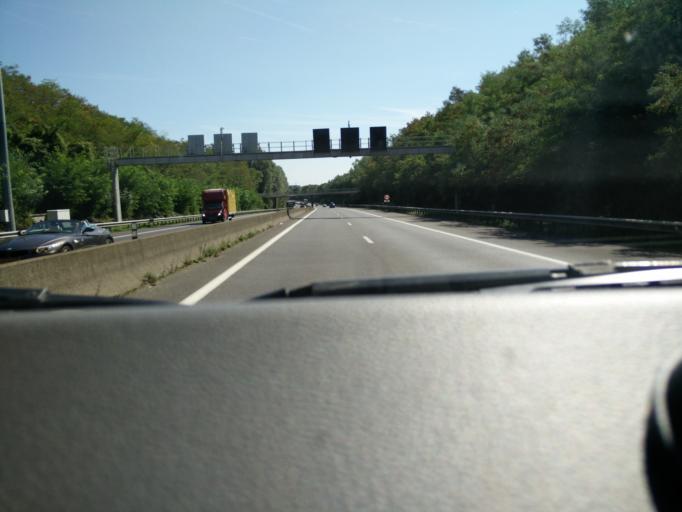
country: LU
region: Luxembourg
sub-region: Canton de Capellen
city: Mamer
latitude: 49.6351
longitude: 6.0287
